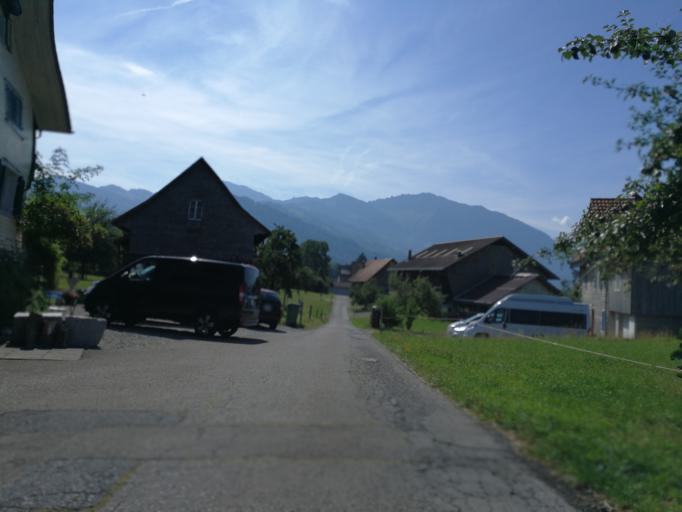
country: CH
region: Saint Gallen
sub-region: Wahlkreis See-Gaster
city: Gommiswald
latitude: 47.2288
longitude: 9.0271
